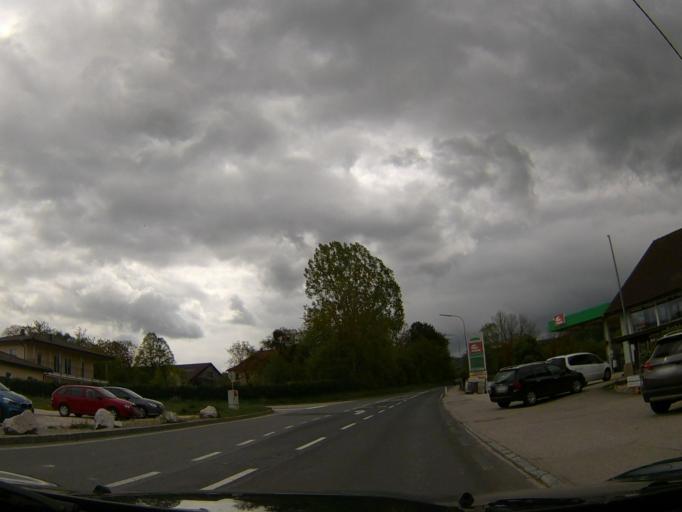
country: AT
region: Upper Austria
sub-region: Politischer Bezirk Vocklabruck
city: Seewalchen
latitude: 47.9446
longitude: 13.5950
